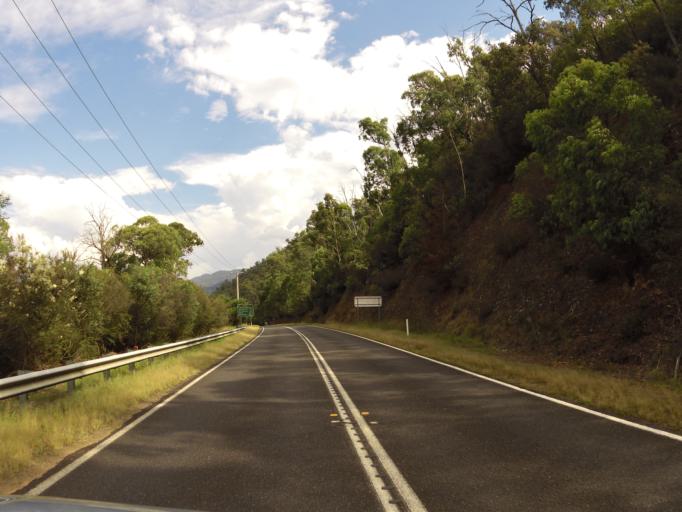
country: AU
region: Victoria
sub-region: Alpine
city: Mount Beauty
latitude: -36.7472
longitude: 147.0163
